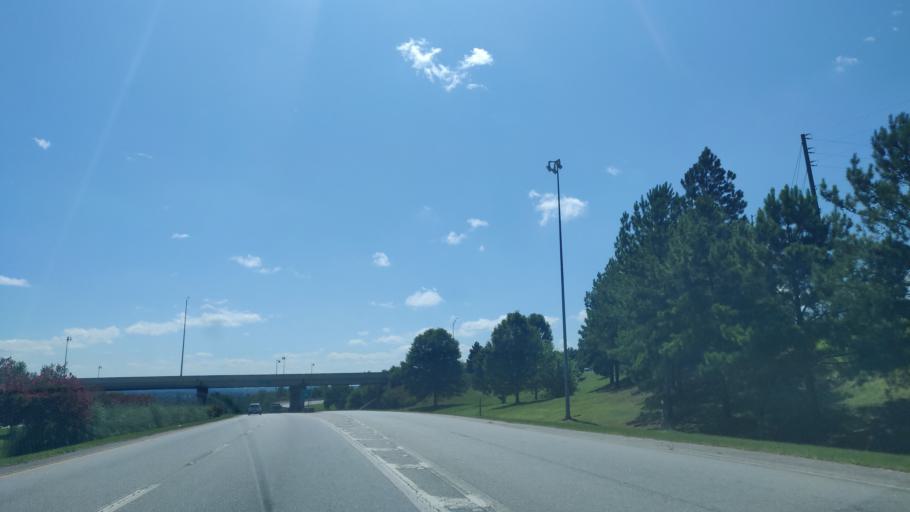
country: US
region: Georgia
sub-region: Muscogee County
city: Columbus
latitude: 32.4529
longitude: -85.0035
